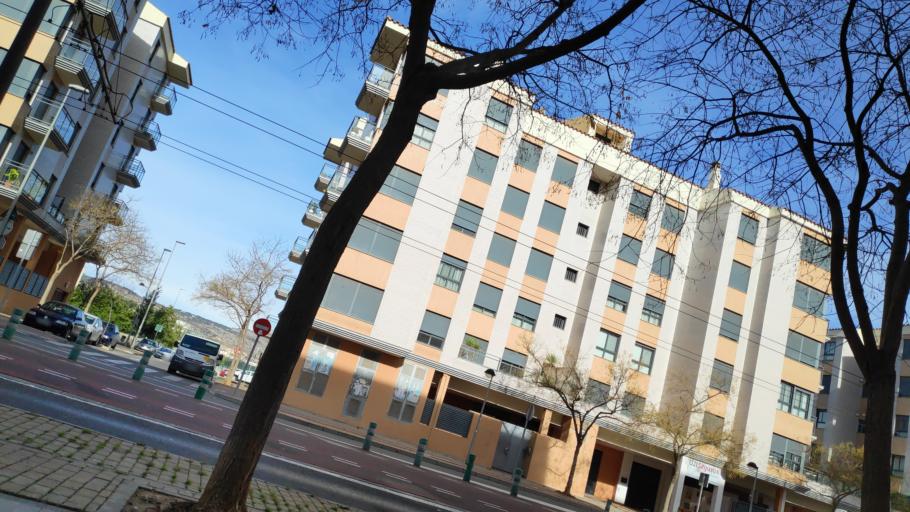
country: ES
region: Valencia
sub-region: Provincia de Castello
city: Castello de la Plana
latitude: 39.9915
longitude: -0.0585
